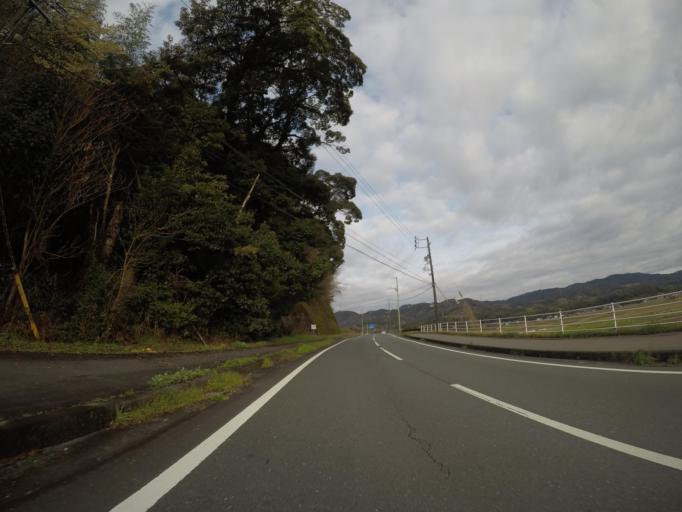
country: JP
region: Shizuoka
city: Hamakita
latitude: 34.8255
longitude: 137.7308
